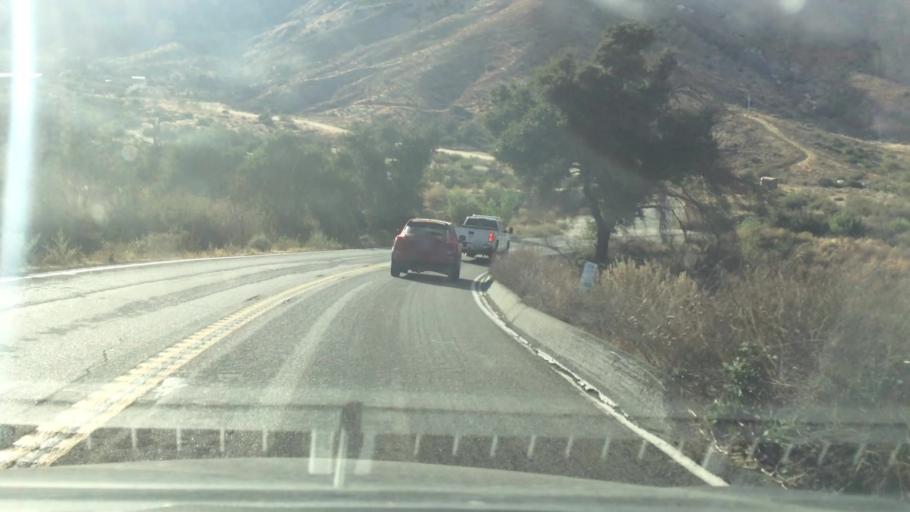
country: US
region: California
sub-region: Riverside County
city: Lakeland Village
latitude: 33.6482
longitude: -117.3759
